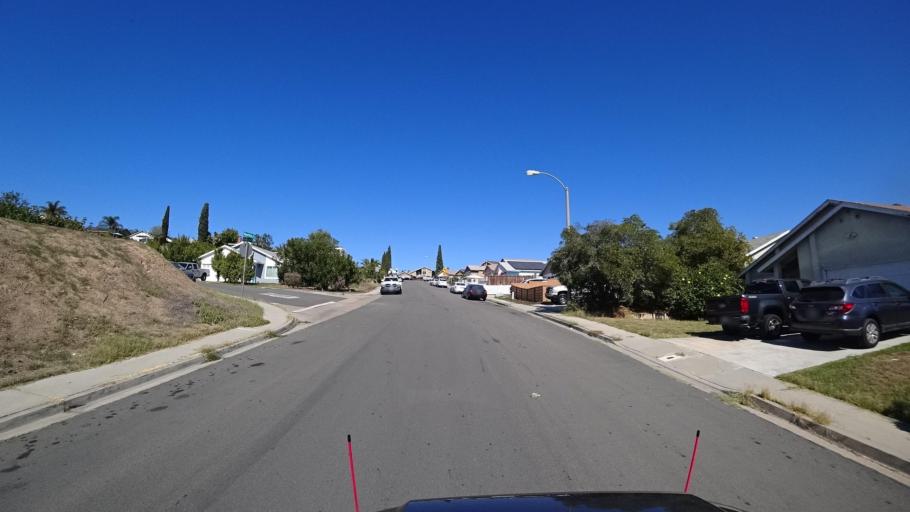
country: US
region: California
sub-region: San Diego County
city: La Presa
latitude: 32.7021
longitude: -117.0208
